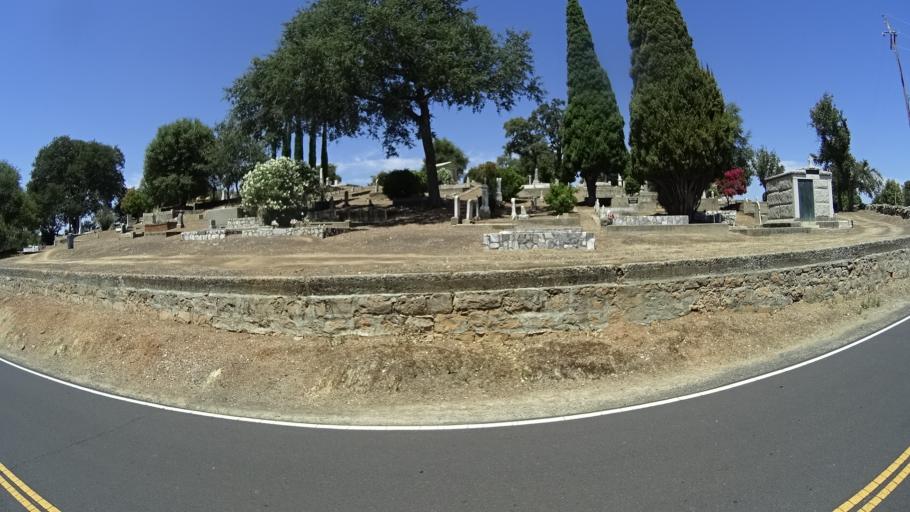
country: US
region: California
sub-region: Calaveras County
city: Angels Camp
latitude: 38.0785
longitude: -120.5584
